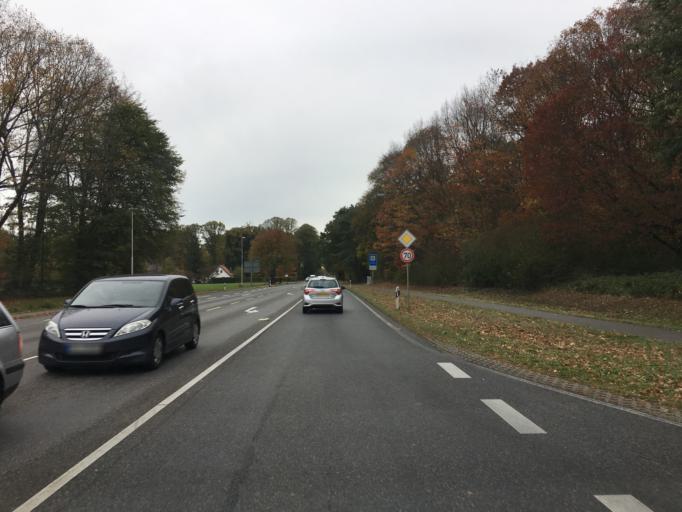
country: DE
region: North Rhine-Westphalia
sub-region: Regierungsbezirk Dusseldorf
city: Emmerich
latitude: 51.8508
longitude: 6.2414
